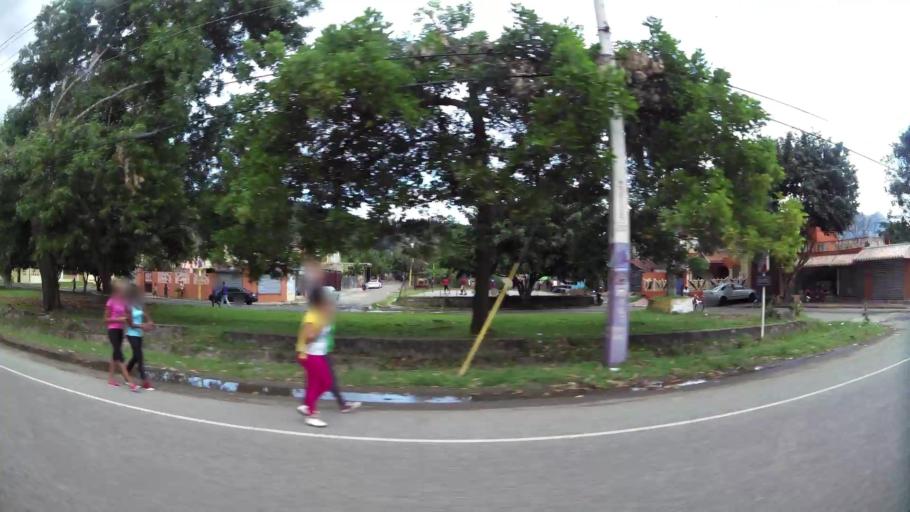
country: DO
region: San Cristobal
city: Villa Altagracia
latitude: 18.6881
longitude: -70.1828
